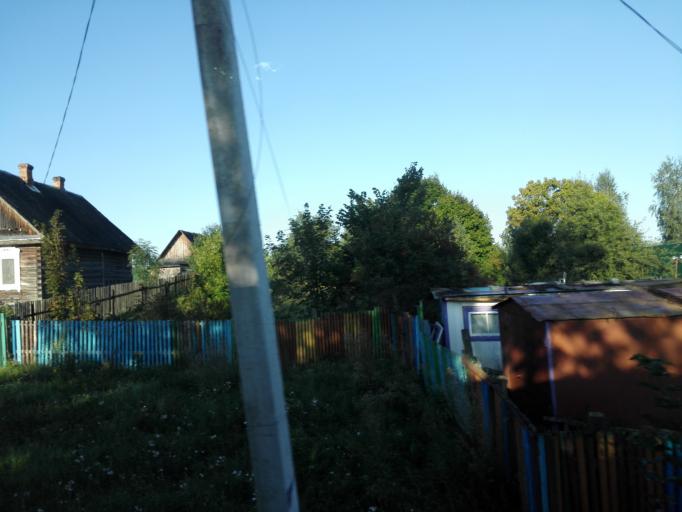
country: BY
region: Mogilev
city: Yalizava
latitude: 53.3271
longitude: 29.0496
